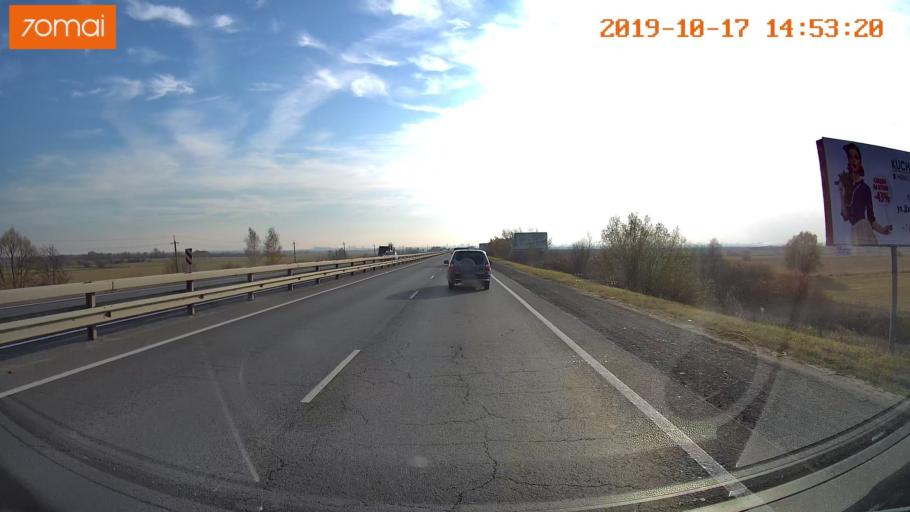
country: RU
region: Rjazan
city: Polyany
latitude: 54.6953
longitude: 39.8389
